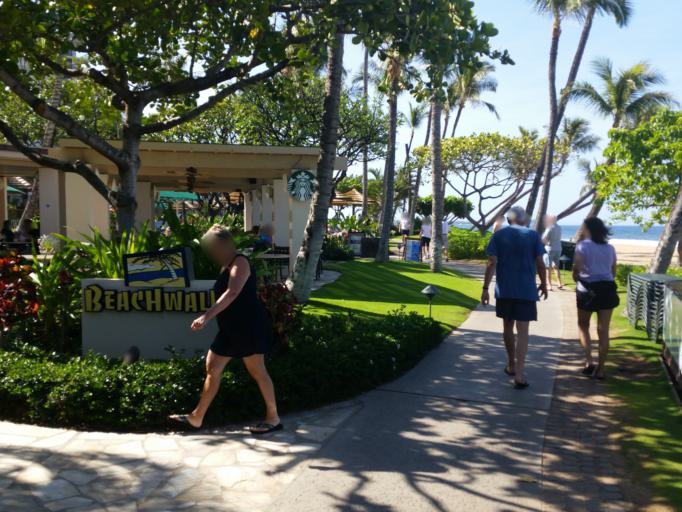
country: US
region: Hawaii
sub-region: Maui County
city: Ka'anapali
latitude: 20.9159
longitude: -156.6962
